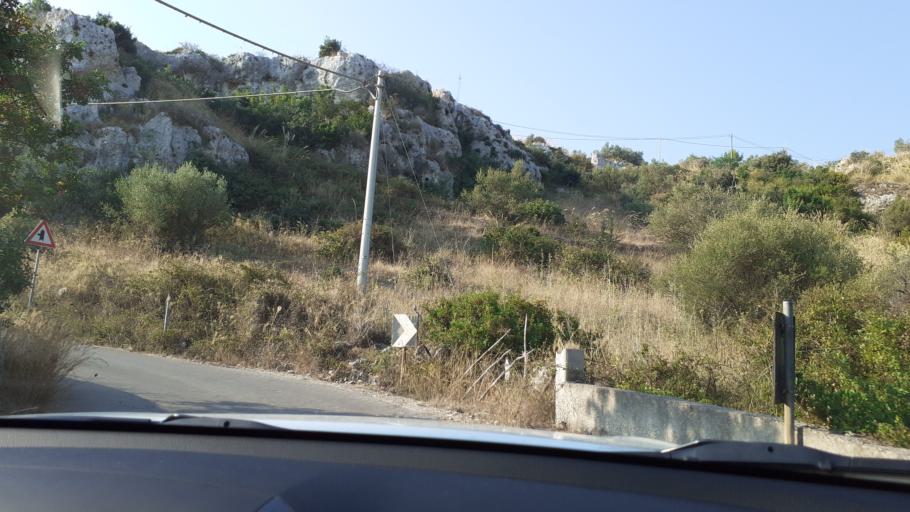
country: IT
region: Sicily
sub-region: Provincia di Siracusa
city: Cassibile
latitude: 36.9784
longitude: 15.1594
